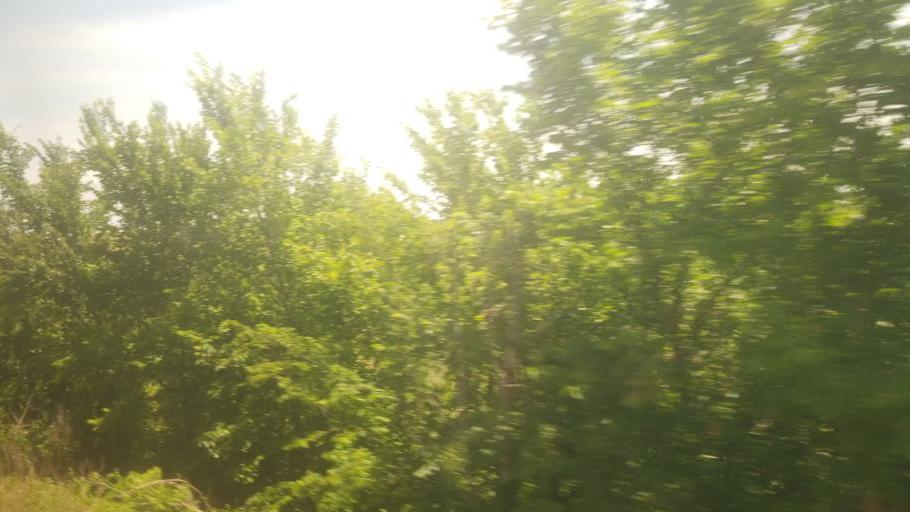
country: US
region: Missouri
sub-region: Linn County
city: Marceline
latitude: 39.8500
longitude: -92.8124
